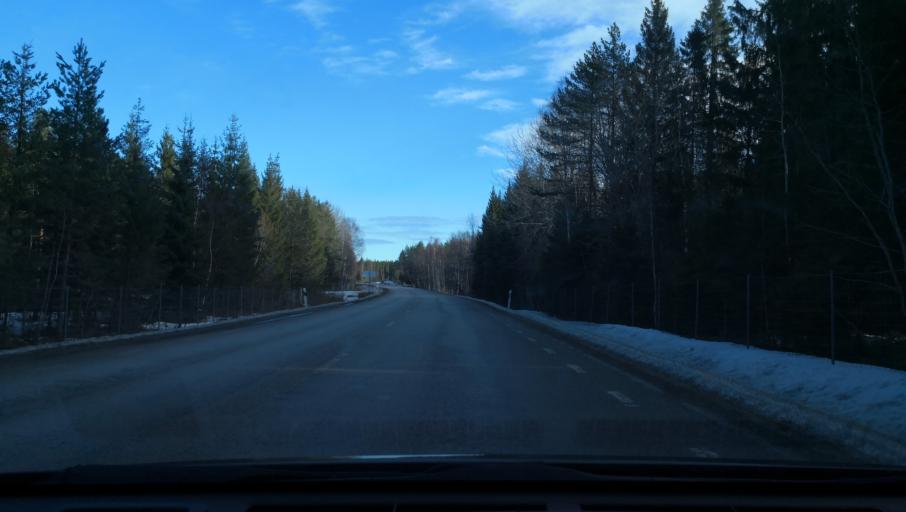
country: SE
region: Uppsala
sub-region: Osthammars Kommun
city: Osterbybruk
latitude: 60.1723
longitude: 17.9284
